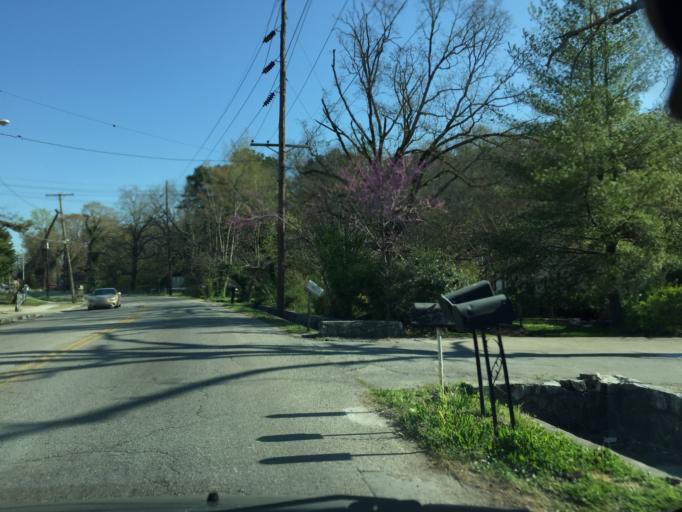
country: US
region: Tennessee
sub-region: Hamilton County
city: East Chattanooga
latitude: 35.0434
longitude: -85.2381
